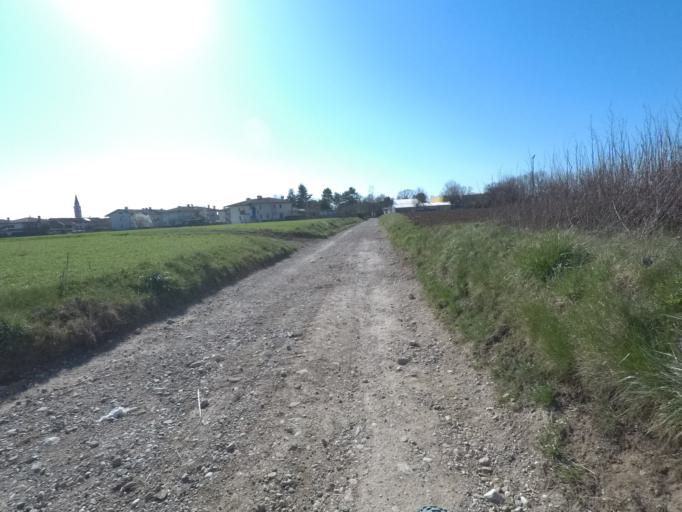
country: IT
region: Friuli Venezia Giulia
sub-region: Provincia di Udine
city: Remanzacco
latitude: 46.0878
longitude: 13.3170
